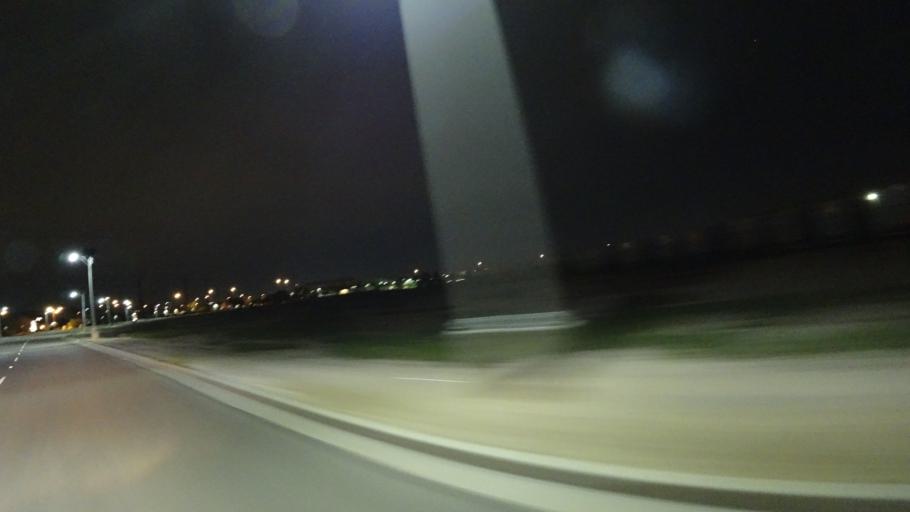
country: US
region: Arizona
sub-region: Maricopa County
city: Guadalupe
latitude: 33.2887
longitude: -111.9619
